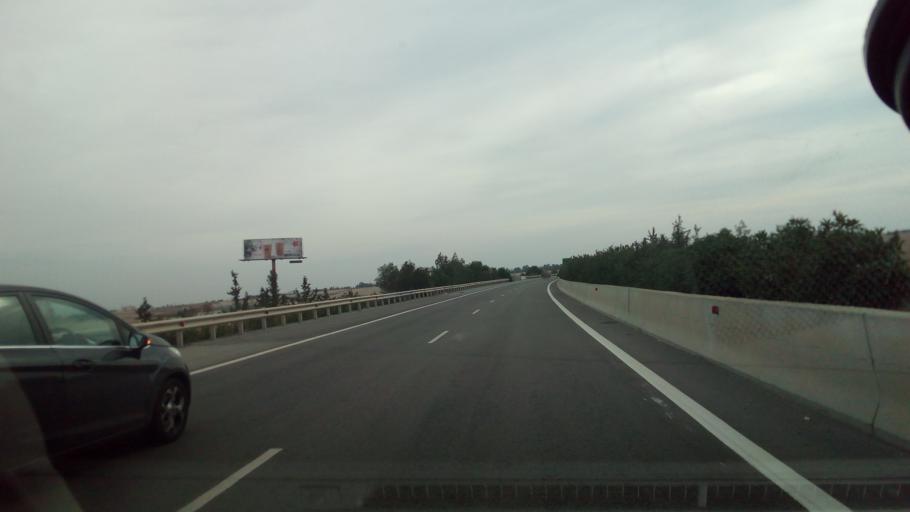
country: CY
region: Larnaka
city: Aradippou
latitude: 34.9208
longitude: 33.5691
